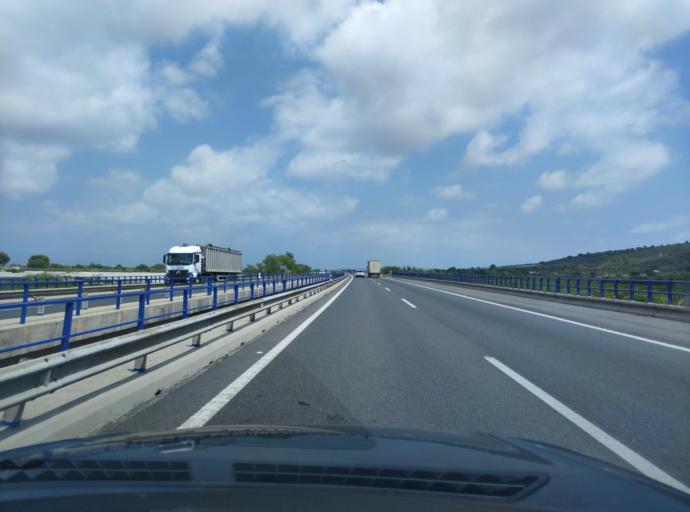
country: ES
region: Valencia
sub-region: Provincia de Castello
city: Vinaros
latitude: 40.5014
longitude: 0.4160
